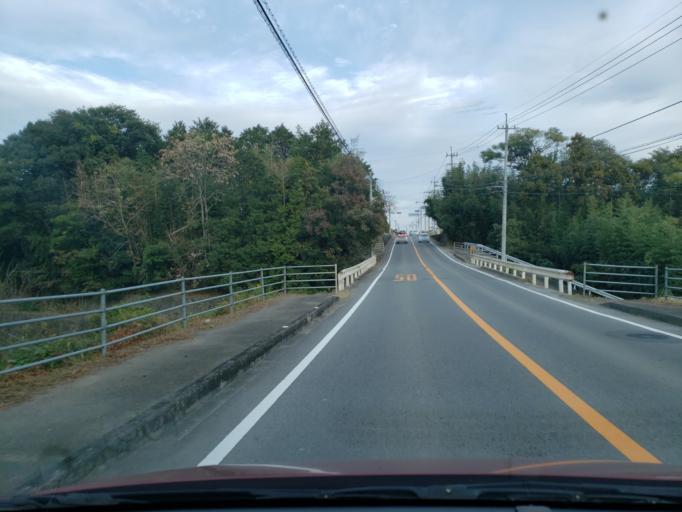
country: JP
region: Tokushima
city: Kamojimacho-jogejima
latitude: 34.0810
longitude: 134.2625
